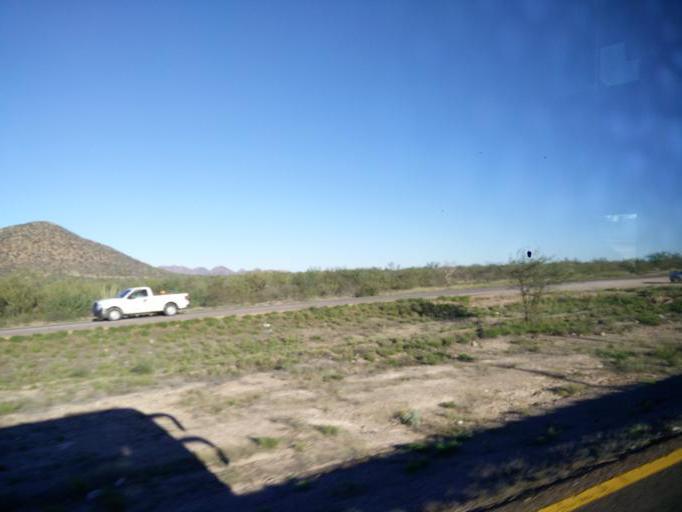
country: MX
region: Sonora
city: Heroica Guaymas
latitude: 28.0112
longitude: -110.9336
